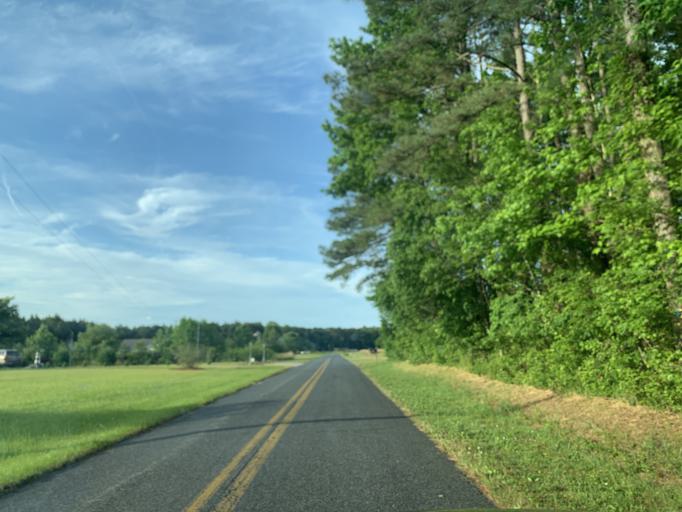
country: US
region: Maryland
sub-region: Worcester County
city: Pocomoke City
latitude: 38.0874
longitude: -75.4657
